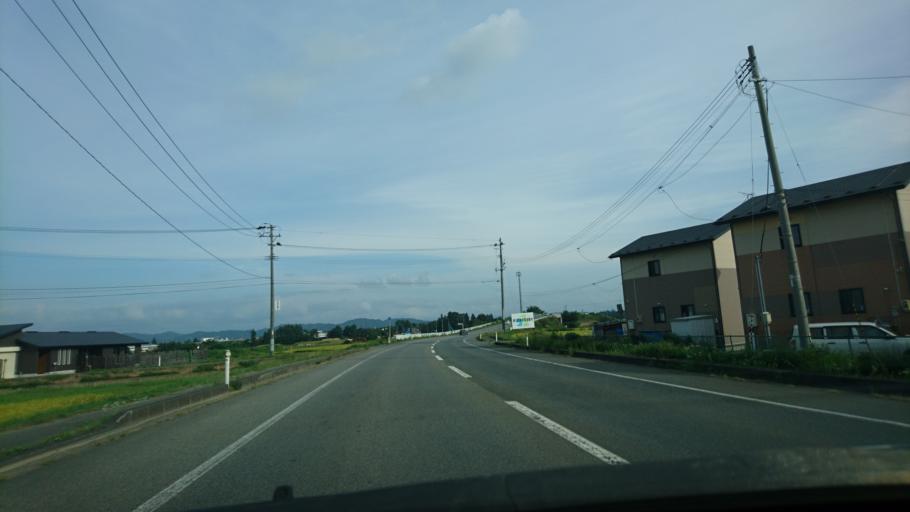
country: JP
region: Iwate
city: Kitakami
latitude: 39.3000
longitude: 141.0805
